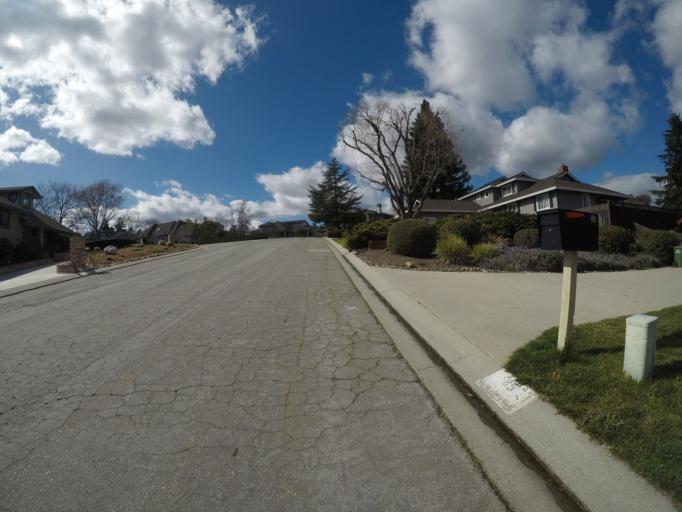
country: US
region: California
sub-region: Santa Cruz County
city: Scotts Valley
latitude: 37.0683
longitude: -122.0090
